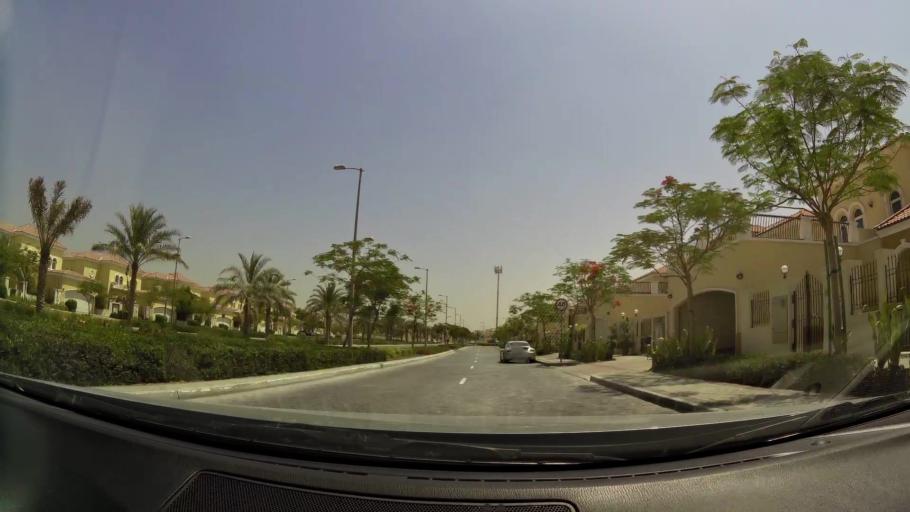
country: AE
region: Dubai
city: Dubai
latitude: 25.0399
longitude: 55.1690
